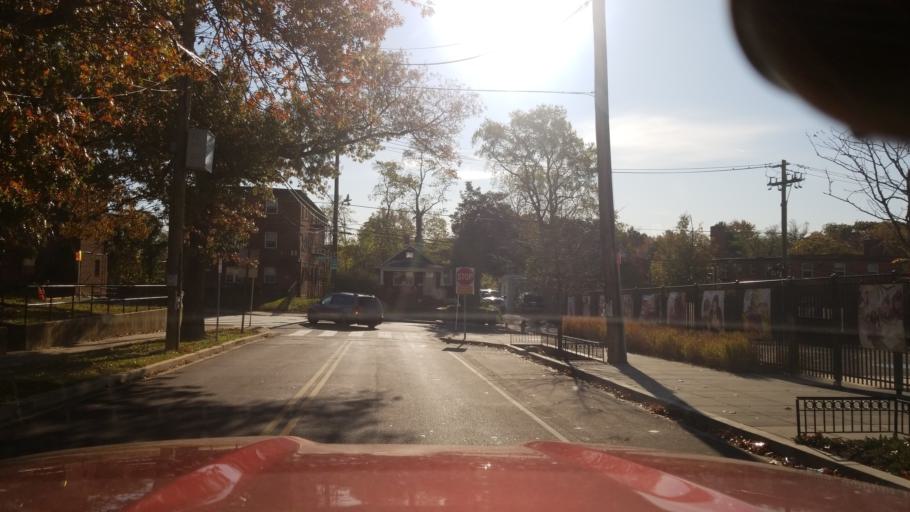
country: US
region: Maryland
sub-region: Prince George's County
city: Hillcrest Heights
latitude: 38.8556
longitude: -76.9738
